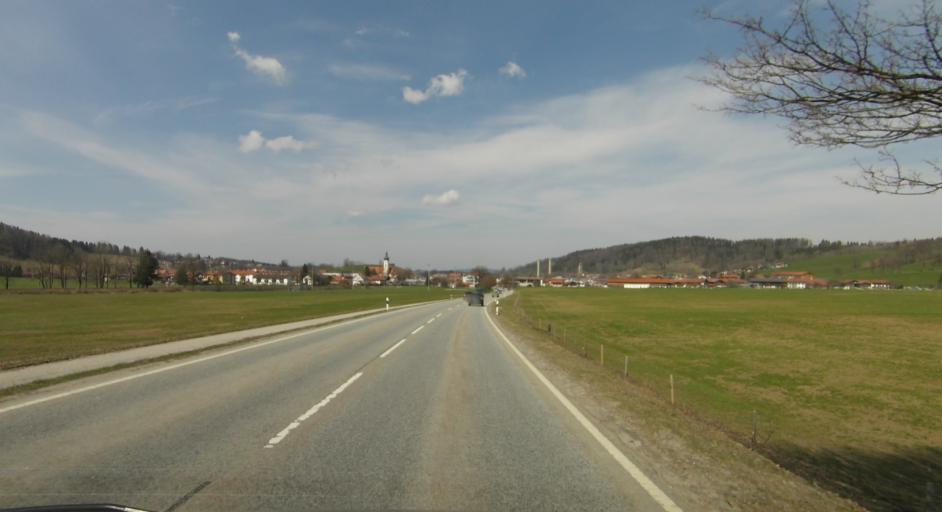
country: DE
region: Bavaria
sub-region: Upper Bavaria
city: Hausham
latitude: 47.7428
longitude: 11.8479
